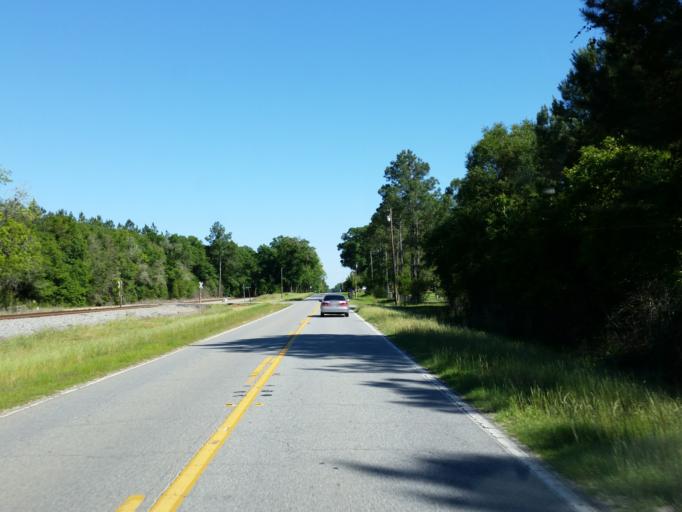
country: US
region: Georgia
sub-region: Echols County
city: Statenville
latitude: 30.6437
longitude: -83.1383
